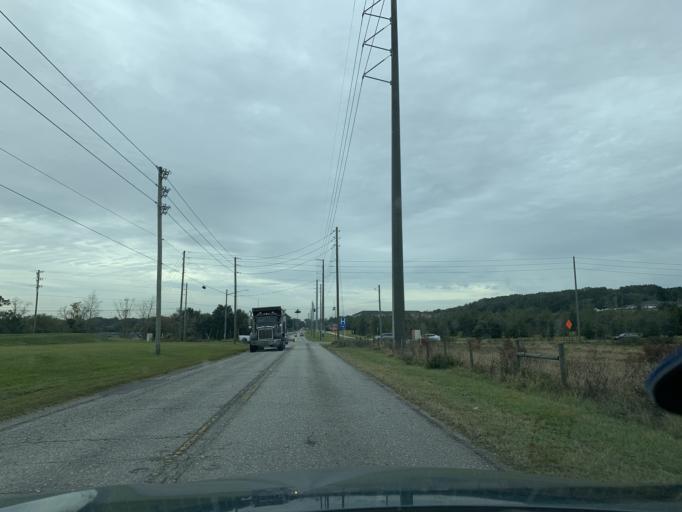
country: US
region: Florida
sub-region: Pasco County
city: Zephyrhills North
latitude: 28.2673
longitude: -82.1799
